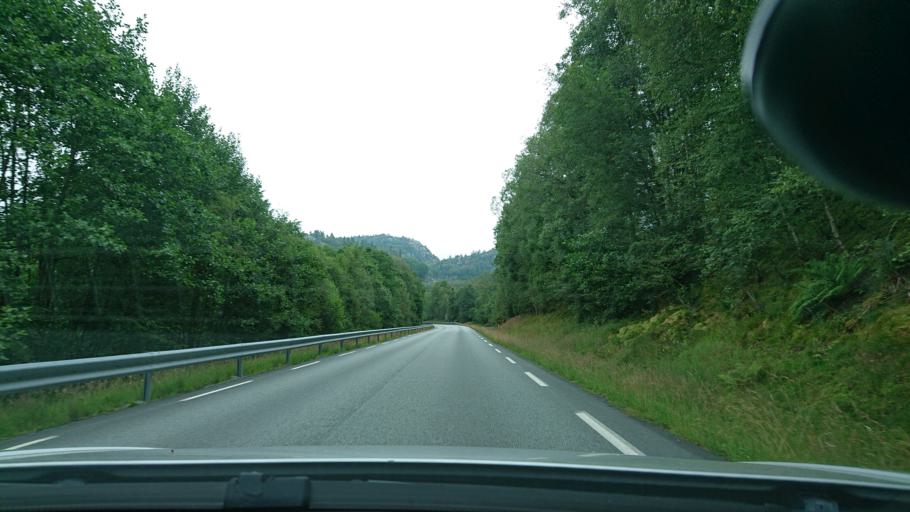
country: NO
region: Rogaland
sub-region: Hjelmeland
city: Hjelmelandsvagen
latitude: 59.2179
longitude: 6.2239
